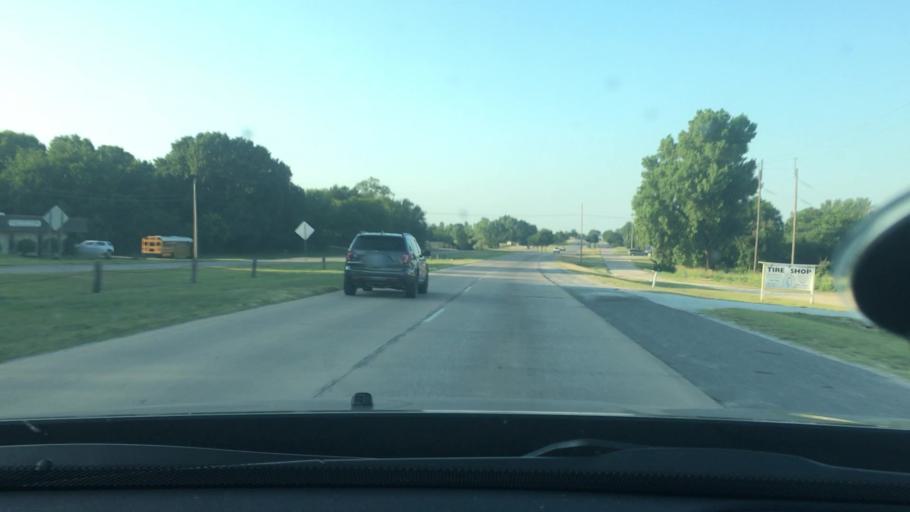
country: US
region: Oklahoma
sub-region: Pontotoc County
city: Ada
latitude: 34.8132
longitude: -96.6786
